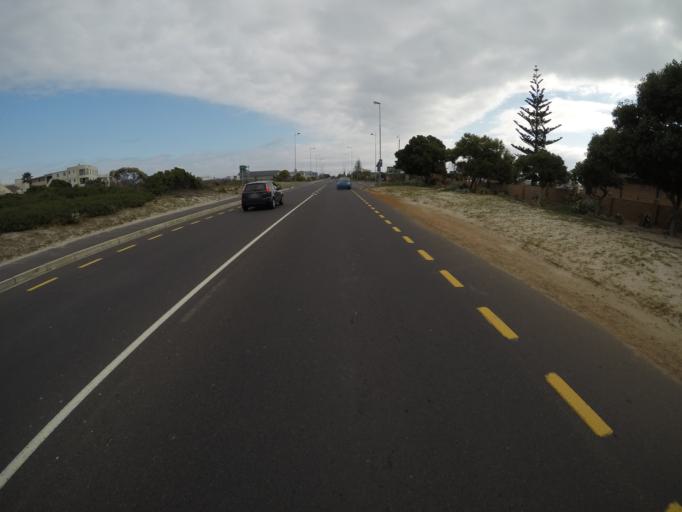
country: ZA
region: Western Cape
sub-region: City of Cape Town
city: Sunset Beach
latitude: -33.7280
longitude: 18.4450
